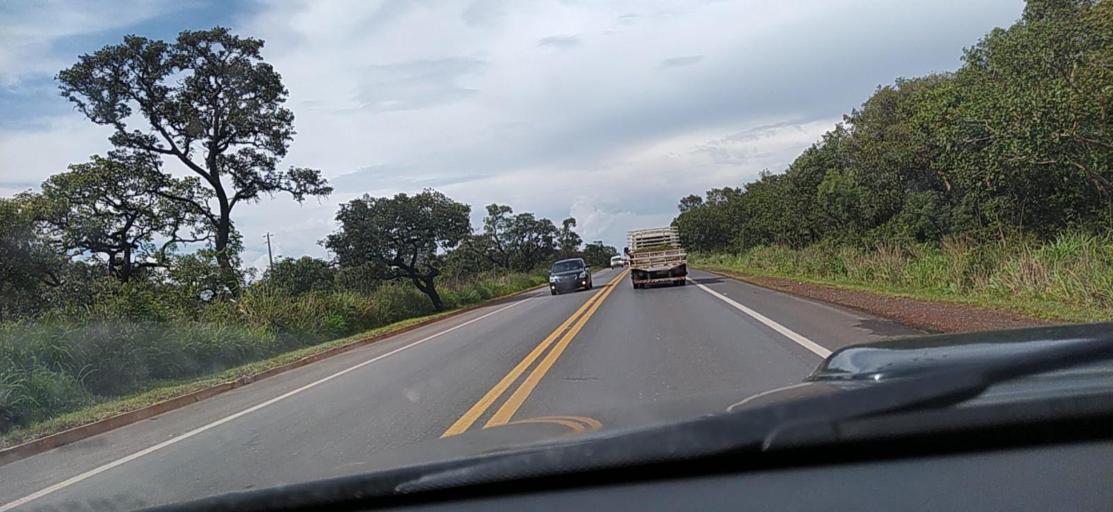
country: BR
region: Minas Gerais
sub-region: Montes Claros
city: Montes Claros
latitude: -16.8655
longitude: -43.8539
